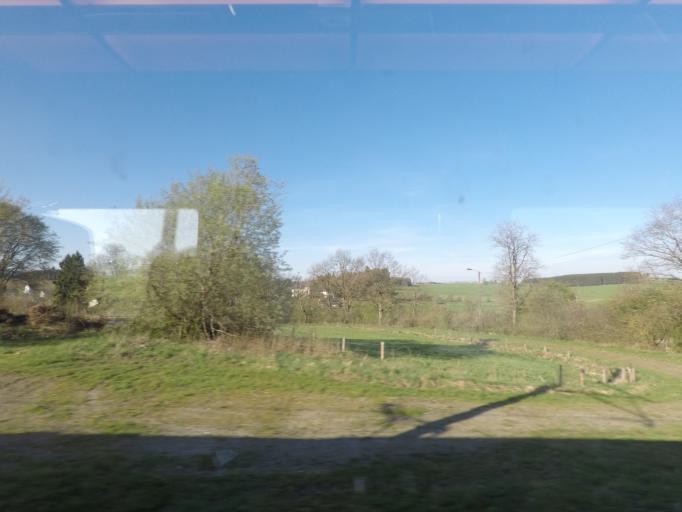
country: BE
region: Wallonia
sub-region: Province du Luxembourg
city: Neufchateau
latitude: 49.8129
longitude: 5.4820
